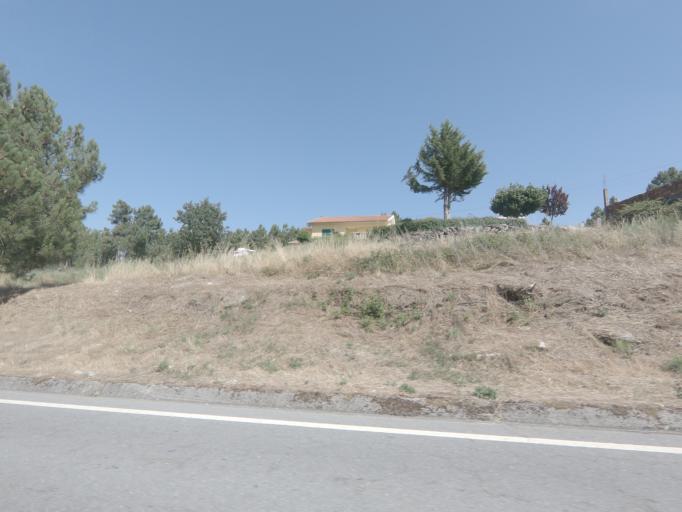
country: PT
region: Viseu
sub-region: Tarouca
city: Tarouca
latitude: 41.0106
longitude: -7.7004
